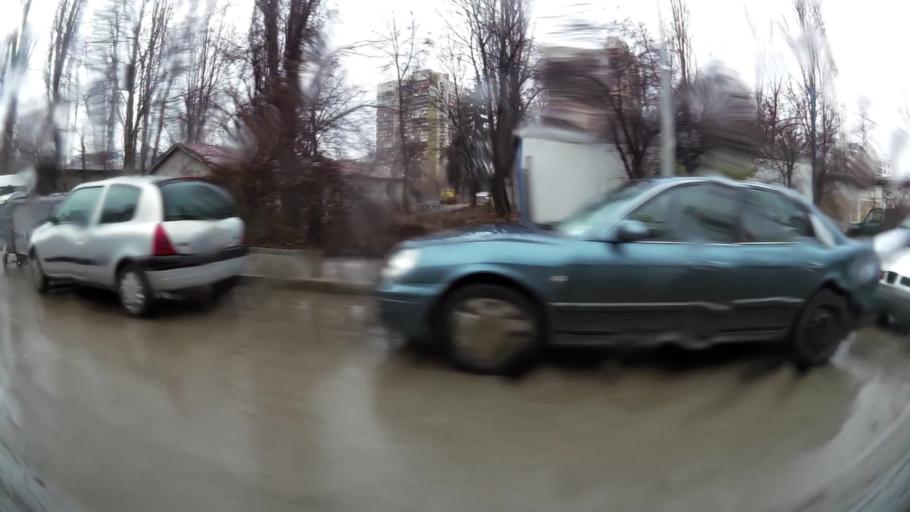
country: BG
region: Sofia-Capital
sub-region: Stolichna Obshtina
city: Sofia
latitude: 42.6606
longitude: 23.3529
